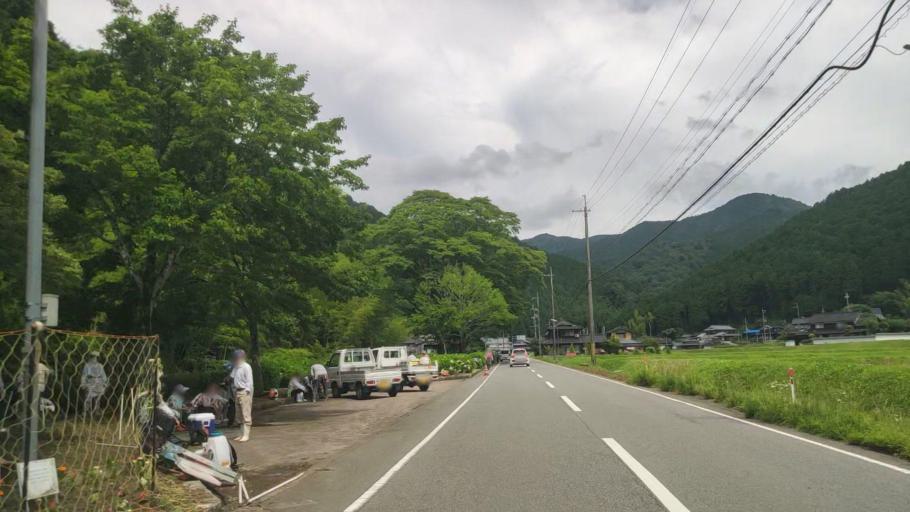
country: JP
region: Hyogo
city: Nishiwaki
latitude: 35.1842
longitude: 134.9323
